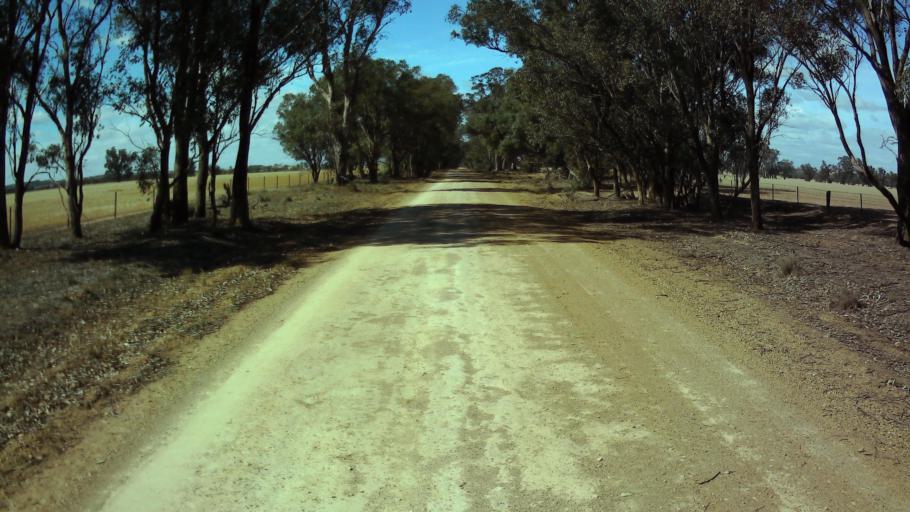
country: AU
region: New South Wales
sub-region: Weddin
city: Grenfell
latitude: -34.0478
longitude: 148.3145
